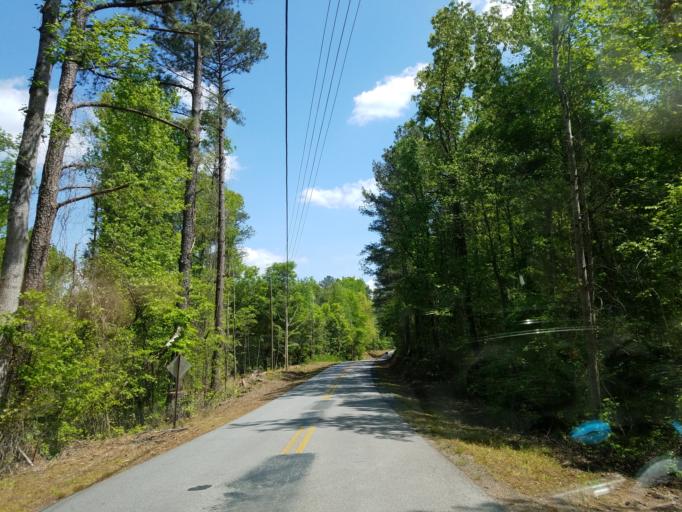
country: US
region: Georgia
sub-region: Monroe County
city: Forsyth
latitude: 33.1238
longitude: -83.9674
